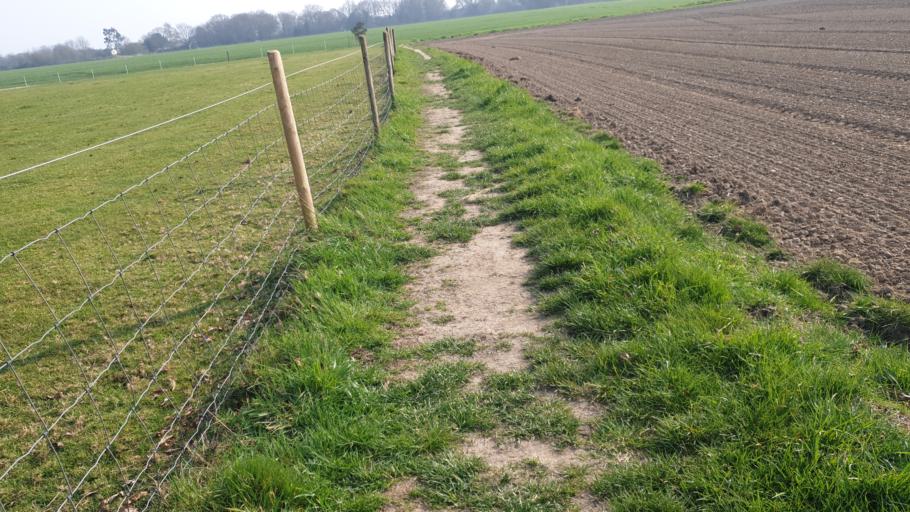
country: GB
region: England
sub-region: Essex
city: Little Clacton
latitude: 51.8798
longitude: 1.1188
